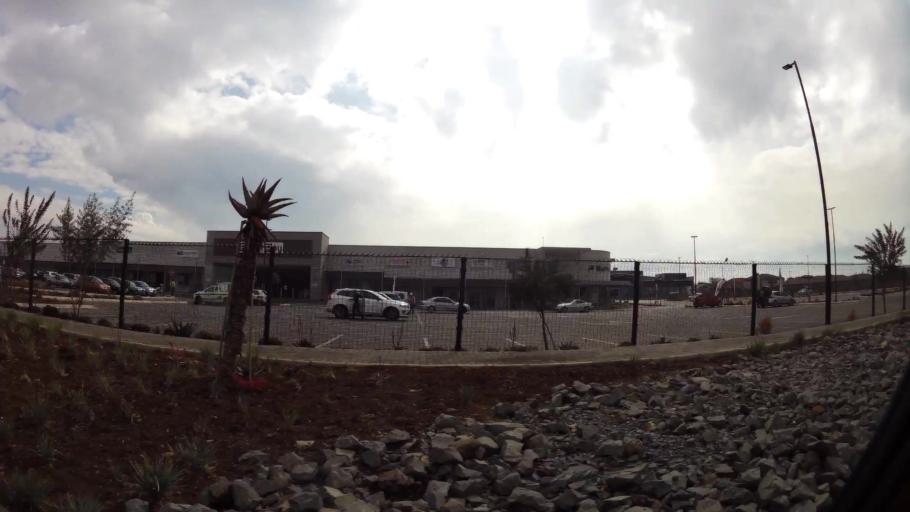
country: ZA
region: Gauteng
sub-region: Sedibeng District Municipality
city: Vanderbijlpark
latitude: -26.7290
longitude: 27.8654
